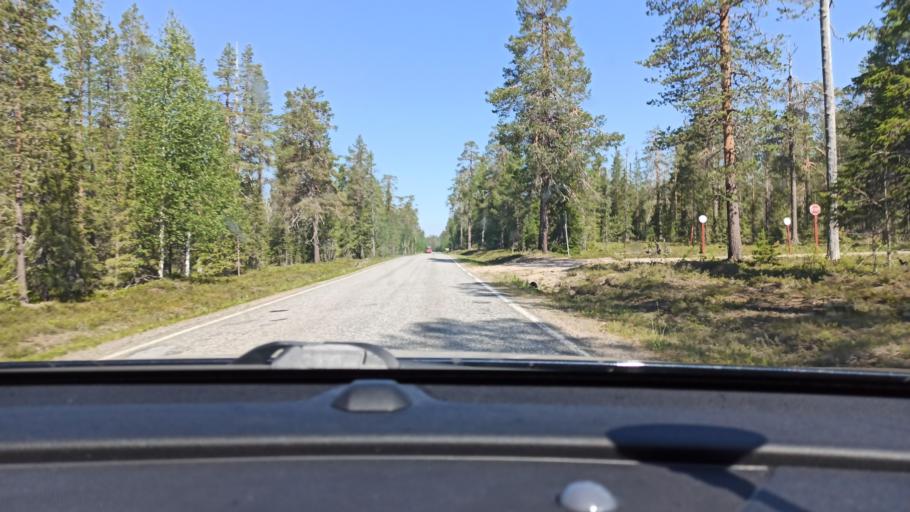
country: FI
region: Lapland
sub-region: Tunturi-Lappi
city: Kolari
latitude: 67.6625
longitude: 24.1645
